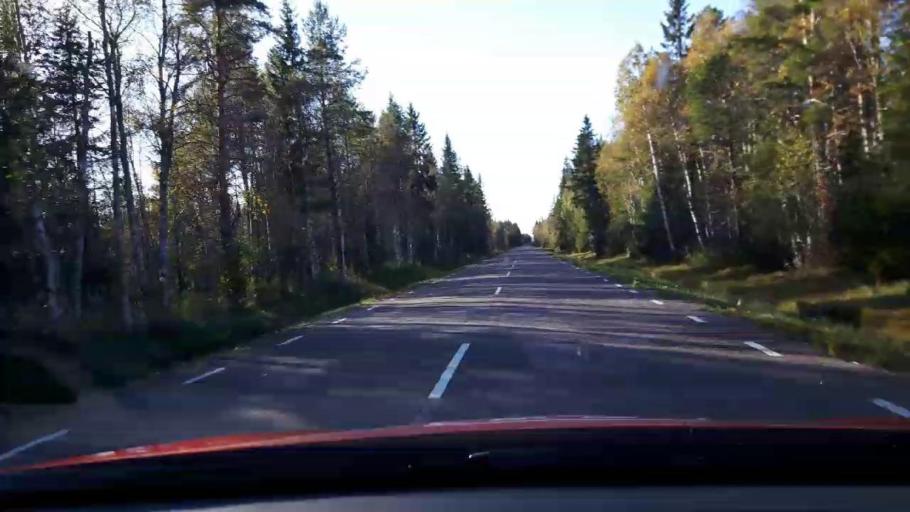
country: SE
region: Jaemtland
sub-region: Stroemsunds Kommun
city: Stroemsund
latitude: 63.8490
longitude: 15.2711
